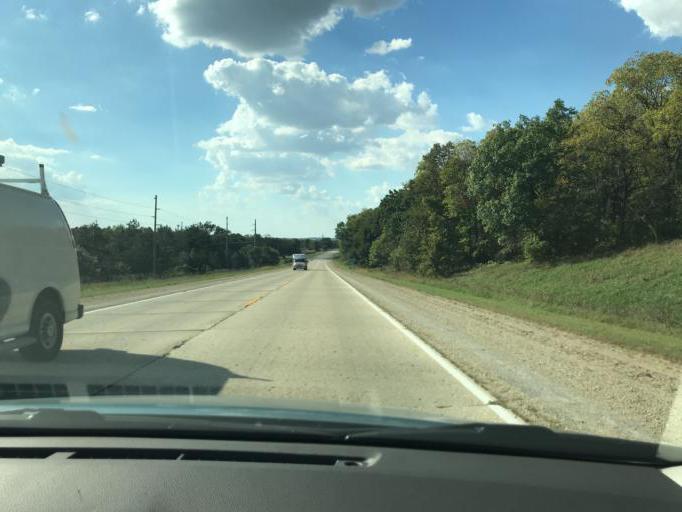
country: US
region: Wisconsin
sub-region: Green County
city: Brodhead
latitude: 42.5629
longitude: -89.3274
